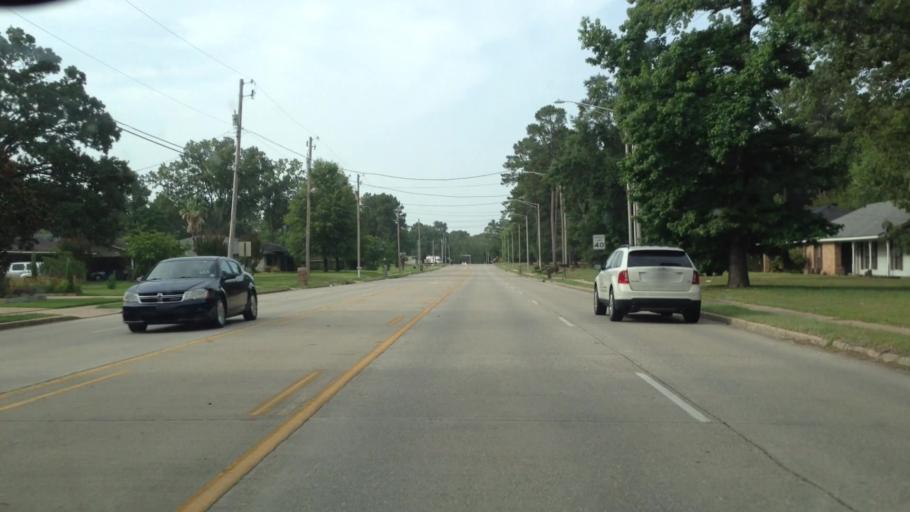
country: US
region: Louisiana
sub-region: De Soto Parish
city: Stonewall
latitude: 32.3989
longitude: -93.8147
